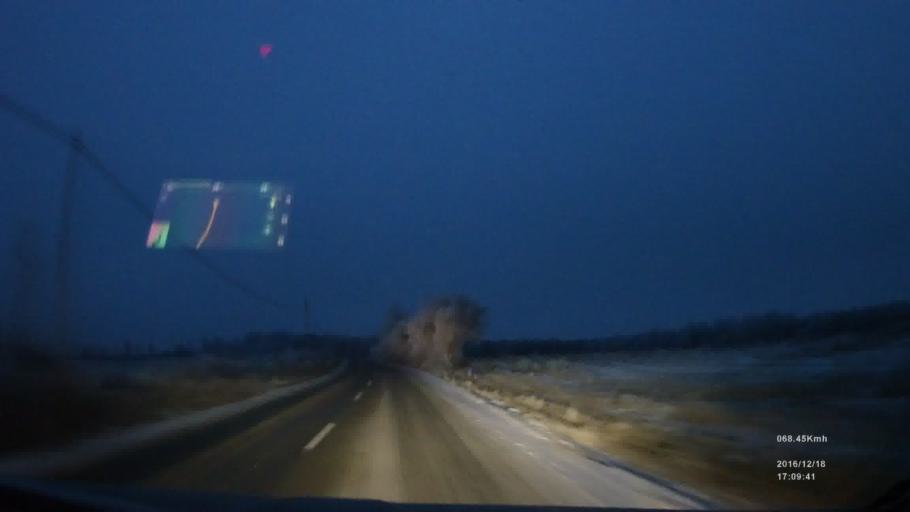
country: SK
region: Presovsky
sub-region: Okres Presov
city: Presov
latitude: 48.8710
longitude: 21.3108
